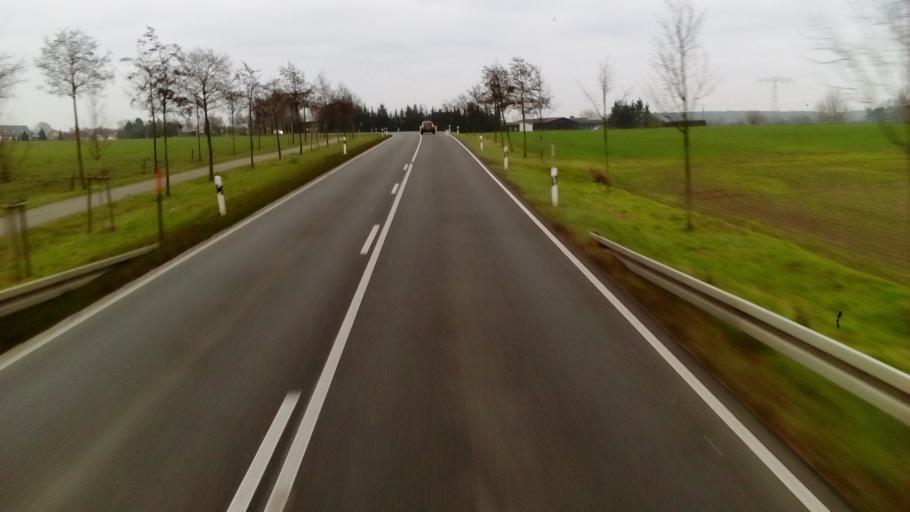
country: DE
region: Mecklenburg-Vorpommern
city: Viereck
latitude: 53.5007
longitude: 14.0482
